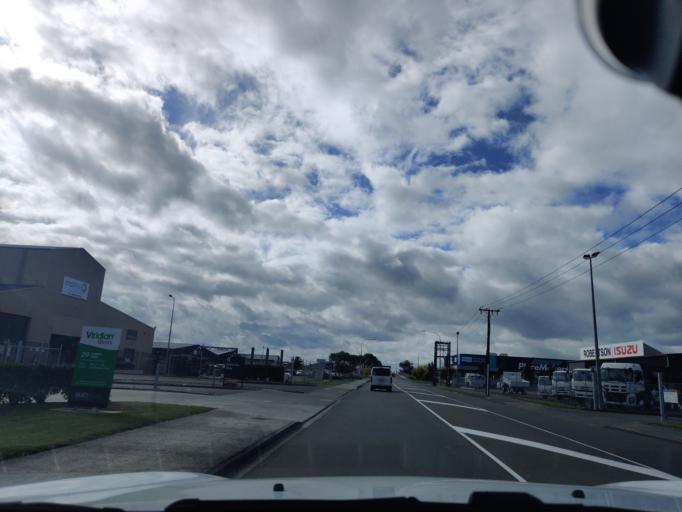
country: NZ
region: Manawatu-Wanganui
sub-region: Palmerston North City
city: Palmerston North
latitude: -40.3289
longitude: 175.6287
